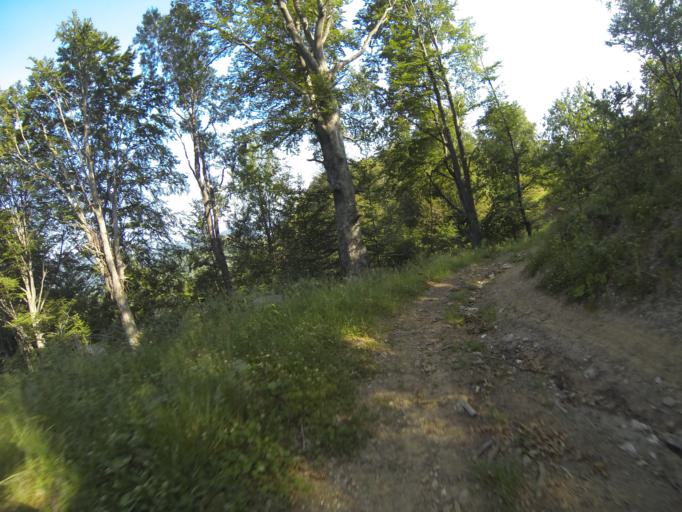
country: RO
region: Valcea
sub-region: Comuna Vaideeni
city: Vaideeni
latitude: 45.2150
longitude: 23.9732
